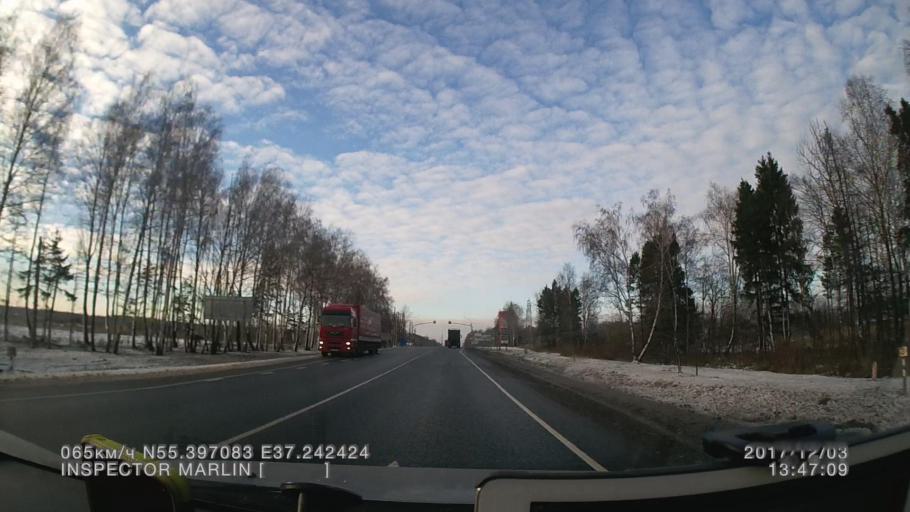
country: RU
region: Moskovskaya
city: Troitsk
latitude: 55.3970
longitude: 37.2426
